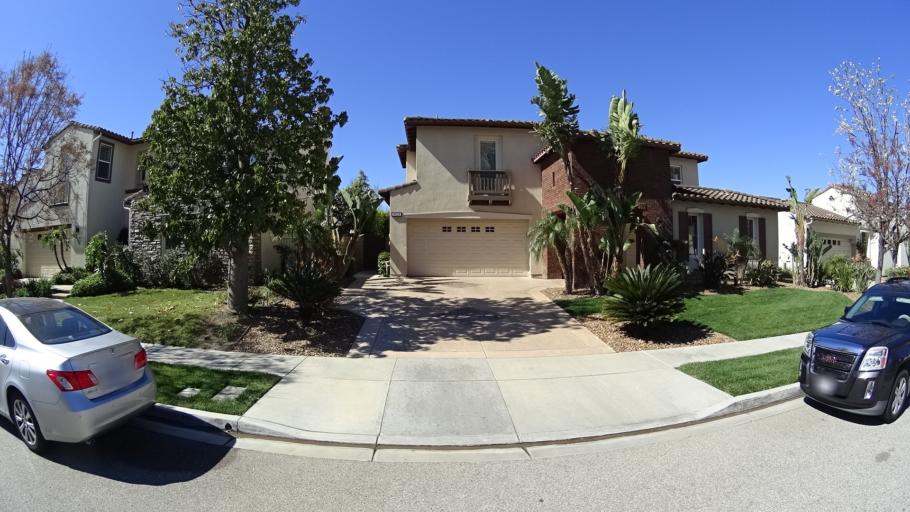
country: US
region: California
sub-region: Ventura County
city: Casa Conejo
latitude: 34.1775
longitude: -118.9820
